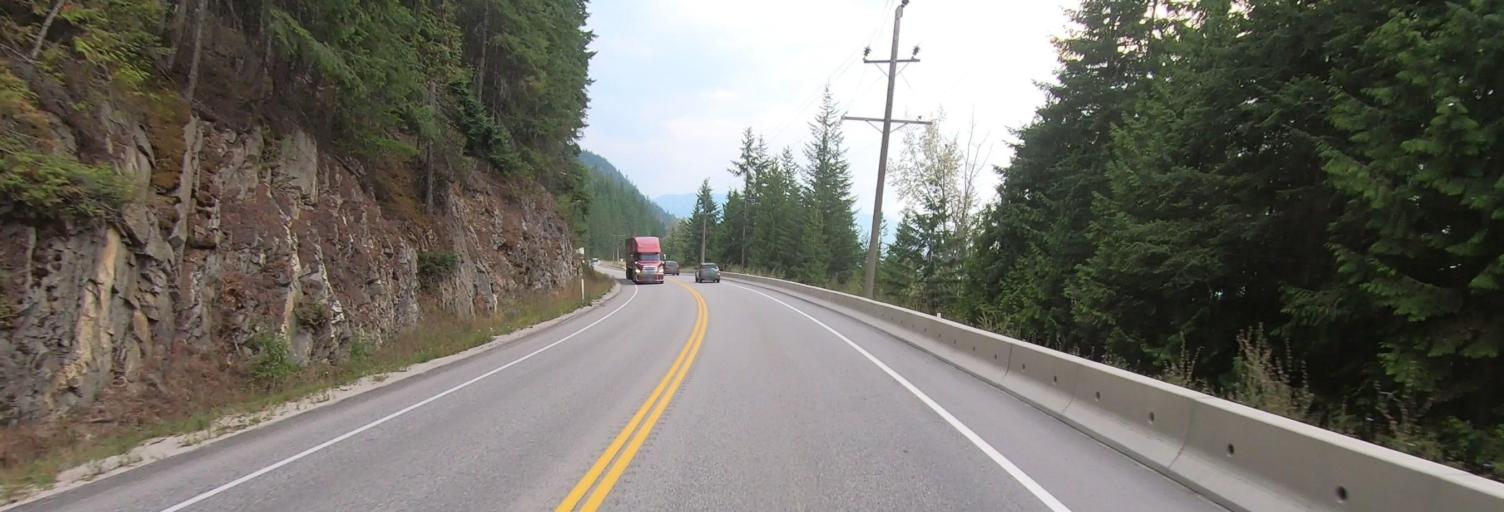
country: CA
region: British Columbia
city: Sicamous
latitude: 50.8173
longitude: -119.0413
